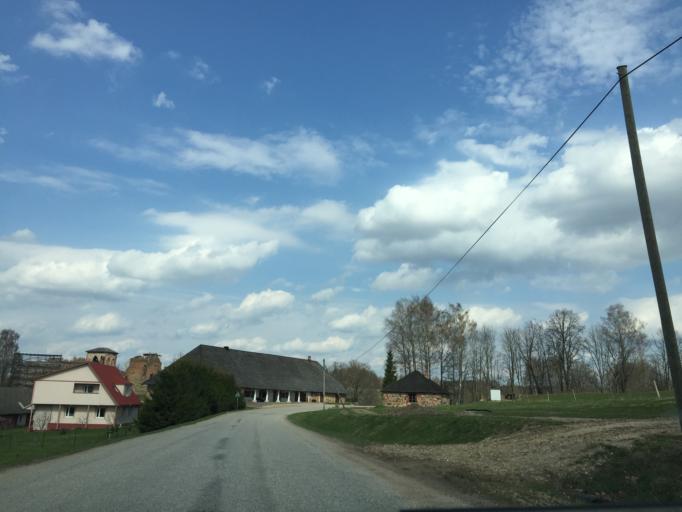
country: RU
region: Pskov
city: Pechory
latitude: 57.7282
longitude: 27.3596
